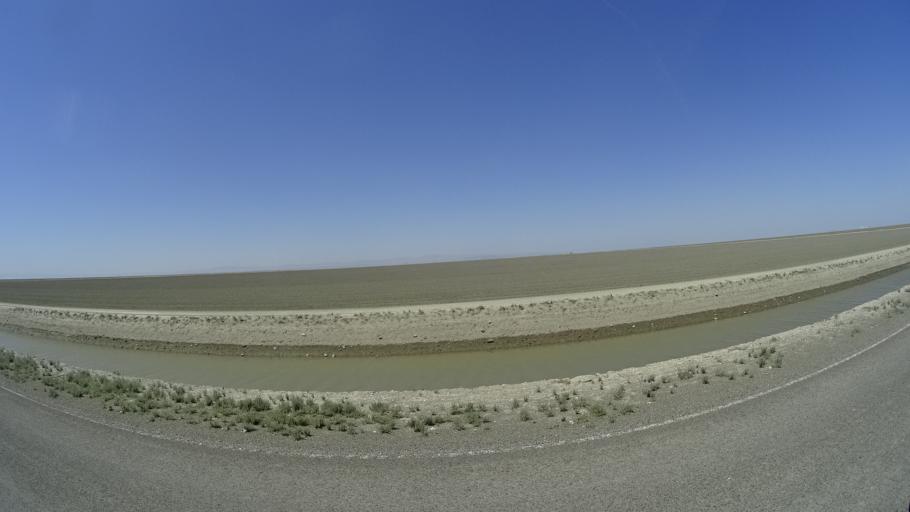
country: US
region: California
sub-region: Kings County
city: Corcoran
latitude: 35.9609
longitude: -119.6461
